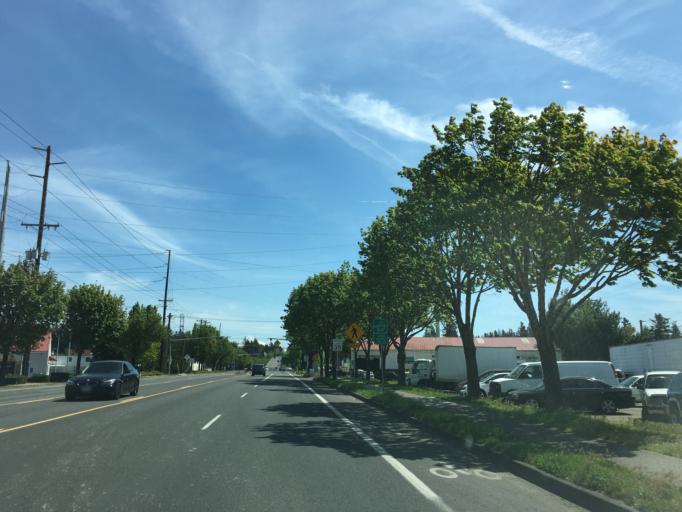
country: US
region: Oregon
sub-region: Multnomah County
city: Gresham
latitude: 45.5157
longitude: -122.4586
